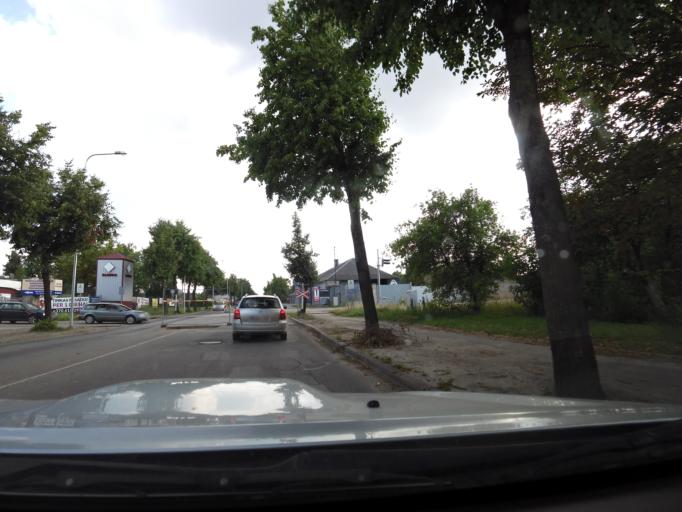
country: LT
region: Siauliu apskritis
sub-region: Siauliai
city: Siauliai
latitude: 55.9514
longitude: 23.3141
